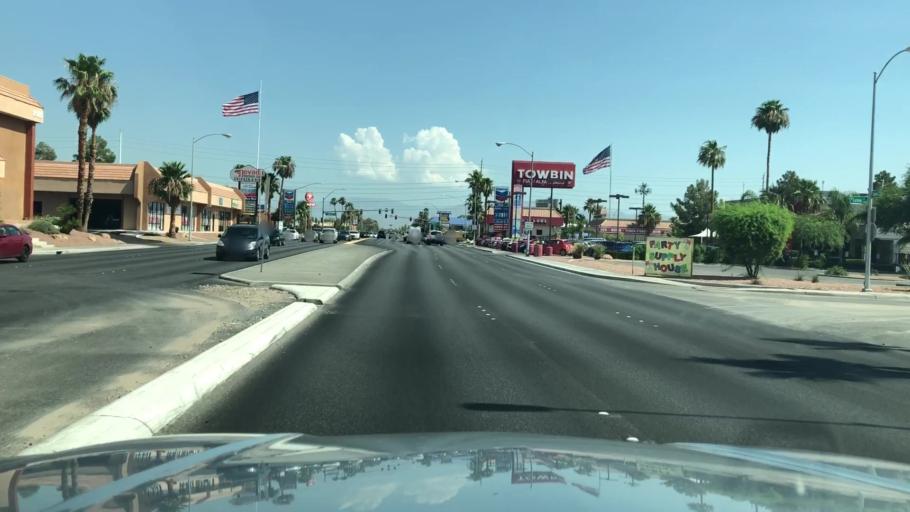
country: US
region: Nevada
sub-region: Clark County
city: Spring Valley
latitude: 36.1421
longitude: -115.2252
